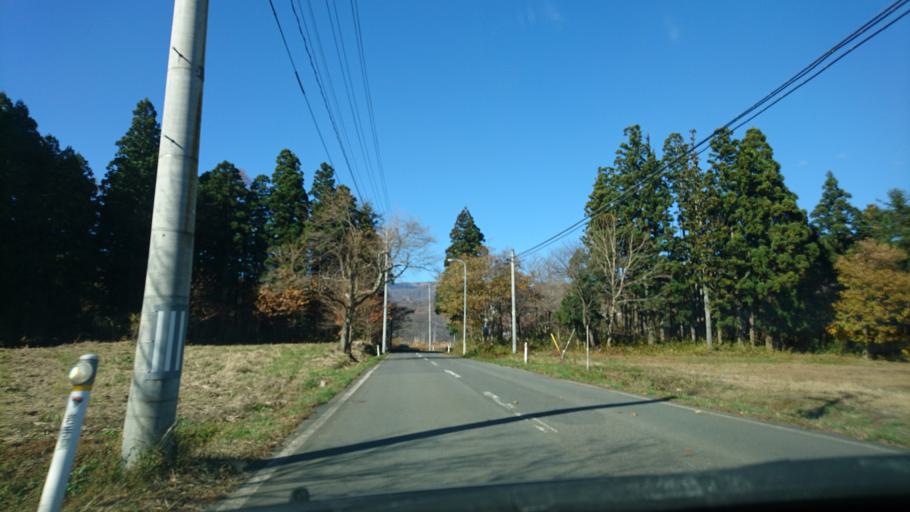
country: JP
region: Iwate
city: Mizusawa
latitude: 39.1183
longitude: 140.9372
